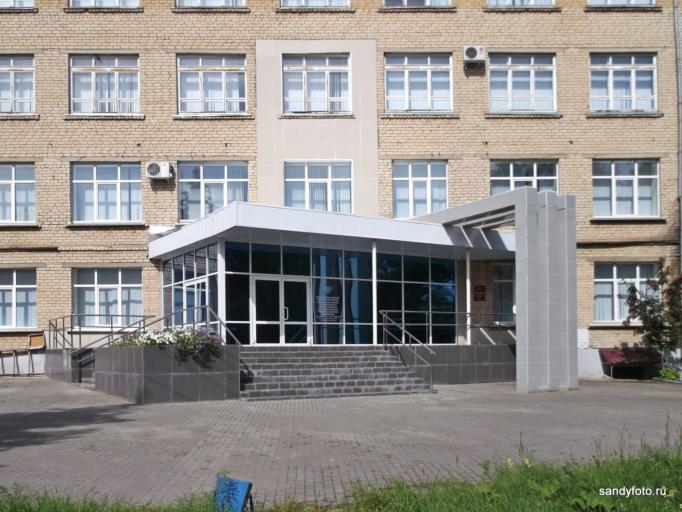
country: RU
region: Chelyabinsk
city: Troitsk
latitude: 54.0820
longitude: 61.5362
